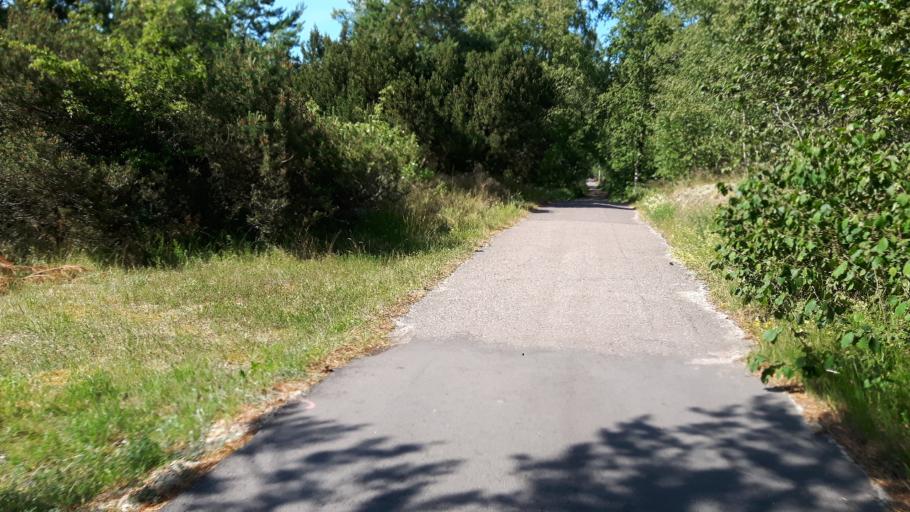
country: LT
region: Klaipedos apskritis
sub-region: Klaipeda
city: Klaipeda
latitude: 55.6879
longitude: 21.1036
